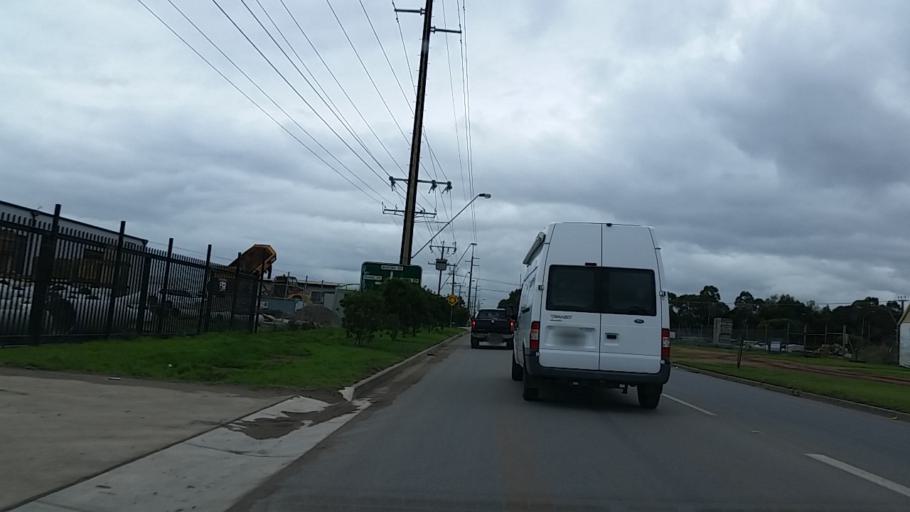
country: AU
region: South Australia
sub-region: Salisbury
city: Salisbury
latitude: -34.7913
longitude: 138.5997
